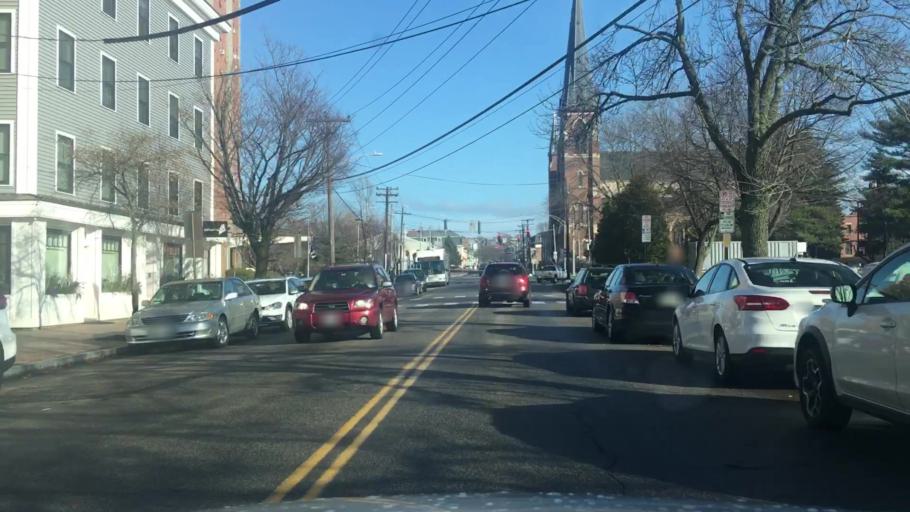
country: US
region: Maine
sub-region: Cumberland County
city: Portland
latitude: 43.6609
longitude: -70.2566
